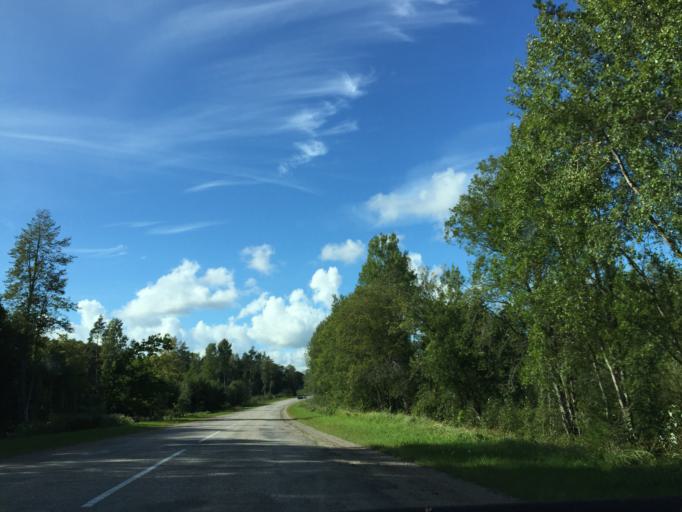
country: LV
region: Kuldigas Rajons
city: Kuldiga
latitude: 56.9895
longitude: 21.7748
